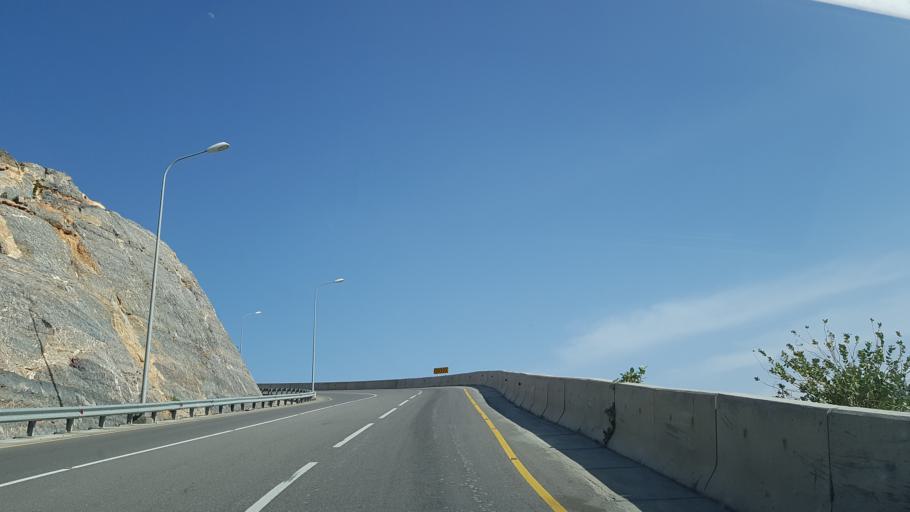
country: OM
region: Muhafazat ad Dakhiliyah
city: Izki
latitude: 23.0656
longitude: 57.7190
